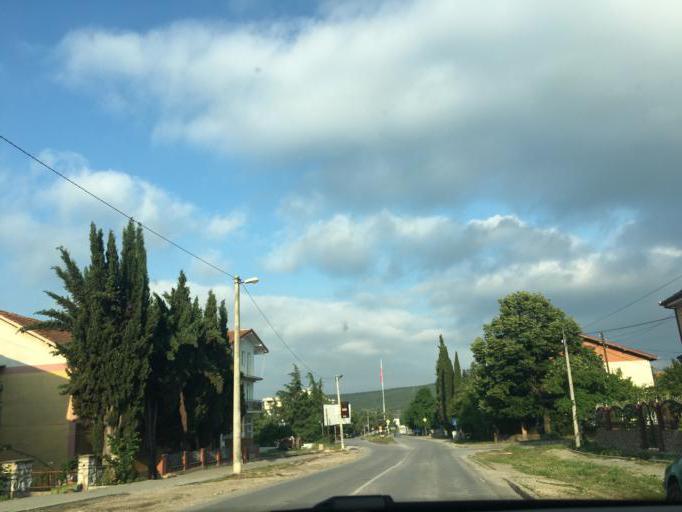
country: MK
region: Valandovo
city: Valandovo
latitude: 41.3158
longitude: 22.5631
